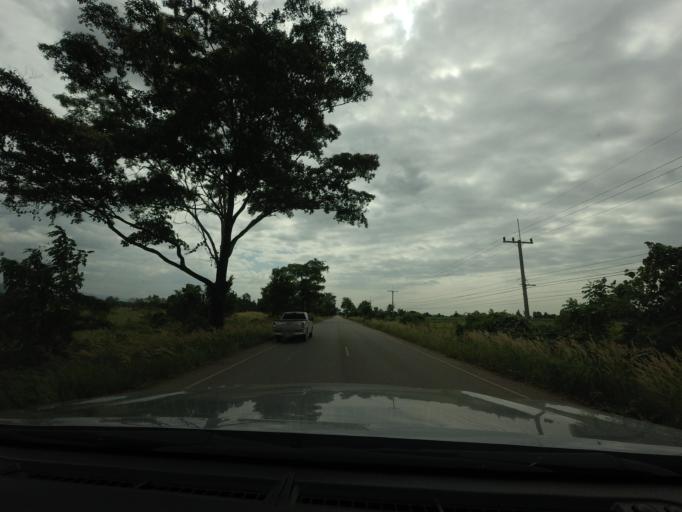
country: TH
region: Phitsanulok
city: Noen Maprang
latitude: 16.6570
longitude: 100.6156
